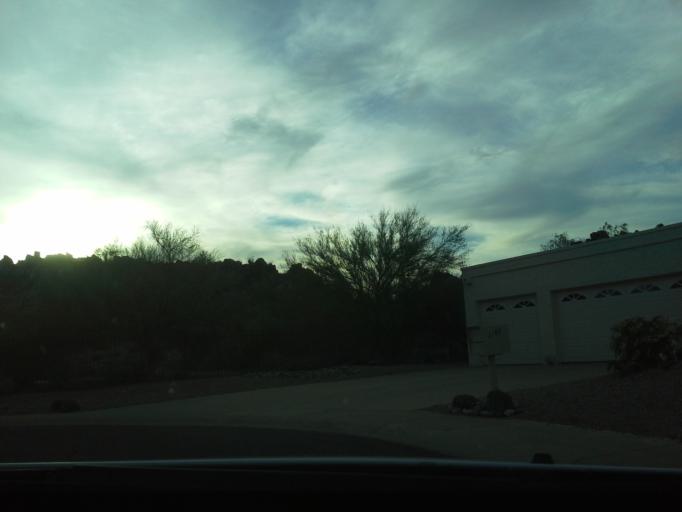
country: US
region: Arizona
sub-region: Maricopa County
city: Paradise Valley
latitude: 33.5675
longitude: -112.0148
